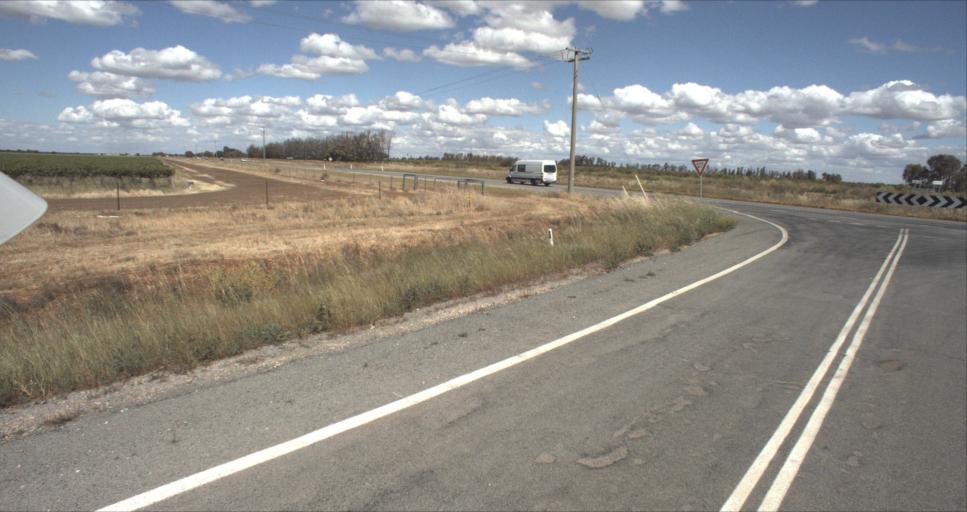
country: AU
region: New South Wales
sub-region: Leeton
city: Leeton
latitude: -34.5039
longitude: 146.2449
